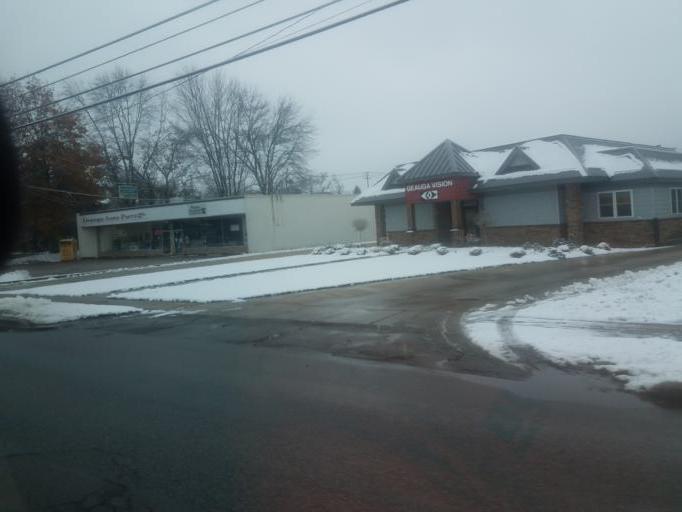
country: US
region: Ohio
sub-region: Geauga County
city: Middlefield
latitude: 41.4632
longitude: -81.0731
